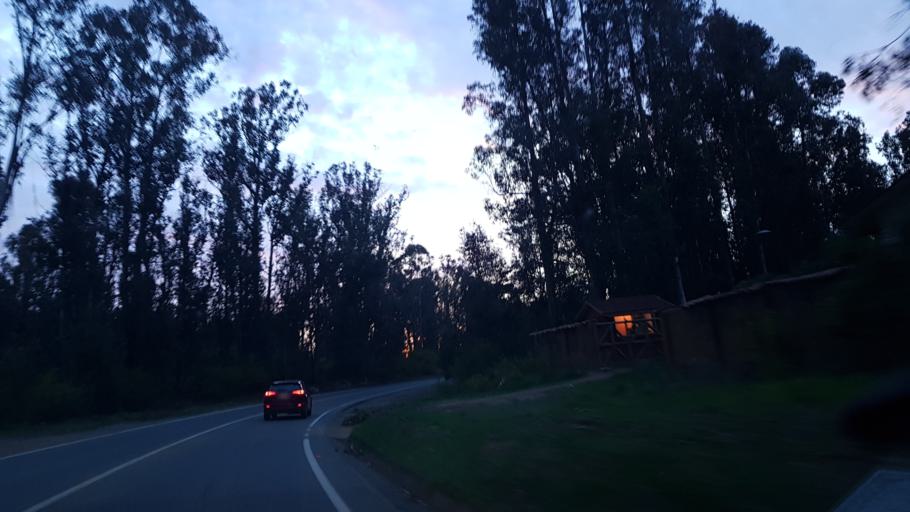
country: CL
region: Valparaiso
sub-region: Provincia de Valparaiso
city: Valparaiso
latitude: -33.0840
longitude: -71.6508
